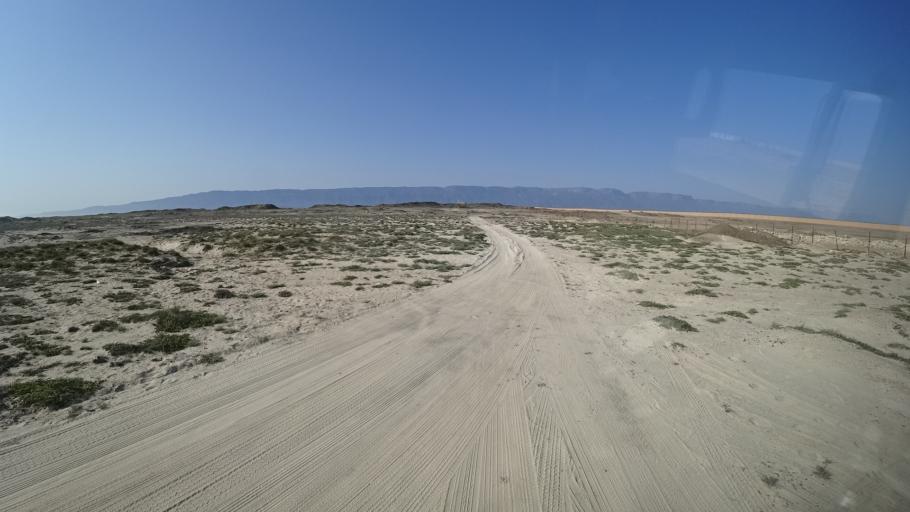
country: OM
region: Zufar
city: Salalah
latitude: 16.9441
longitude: 54.7997
